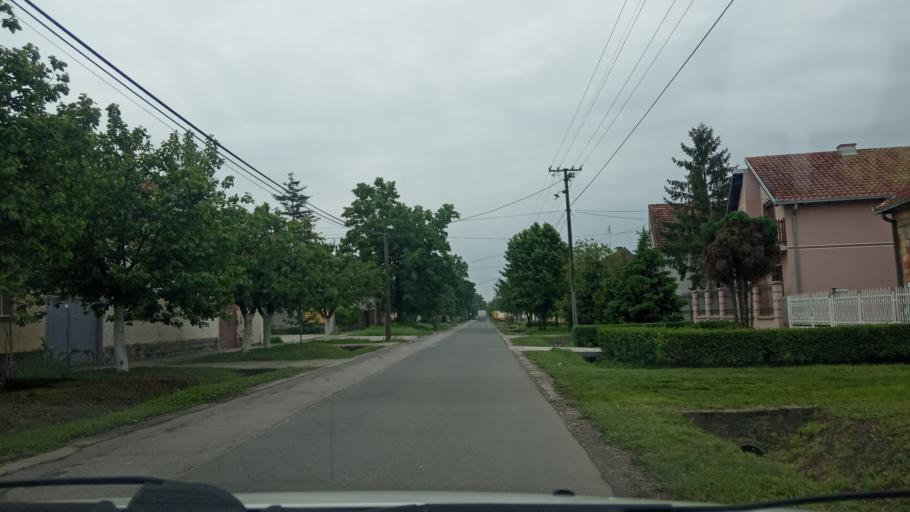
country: RS
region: Autonomna Pokrajina Vojvodina
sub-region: Sremski Okrug
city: Stara Pazova
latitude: 44.9927
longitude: 20.1528
